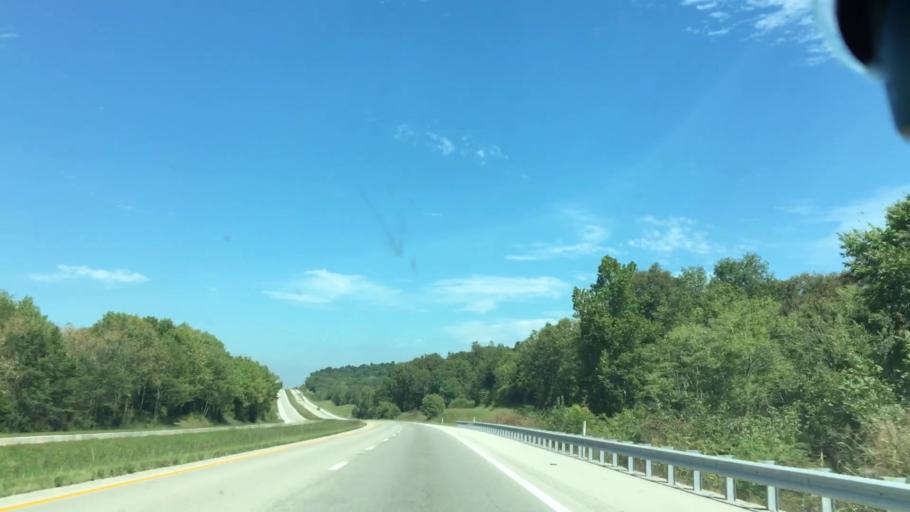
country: US
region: Kentucky
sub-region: Christian County
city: Hopkinsville
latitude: 36.9290
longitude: -87.4706
